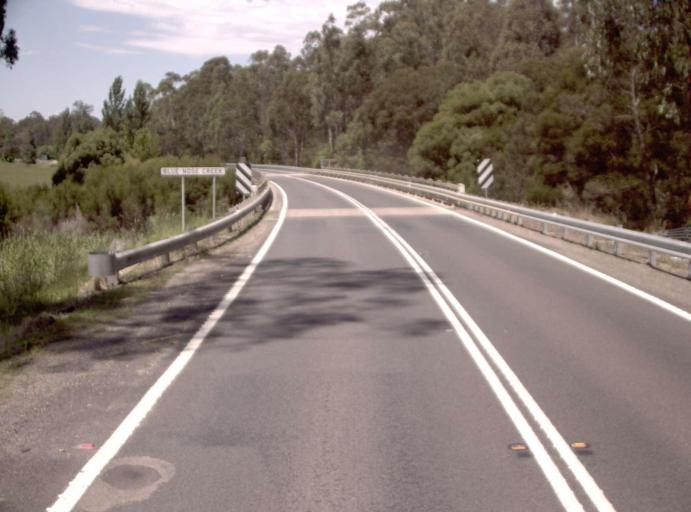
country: AU
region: New South Wales
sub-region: Bombala
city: Bombala
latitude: -37.5706
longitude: 149.1355
